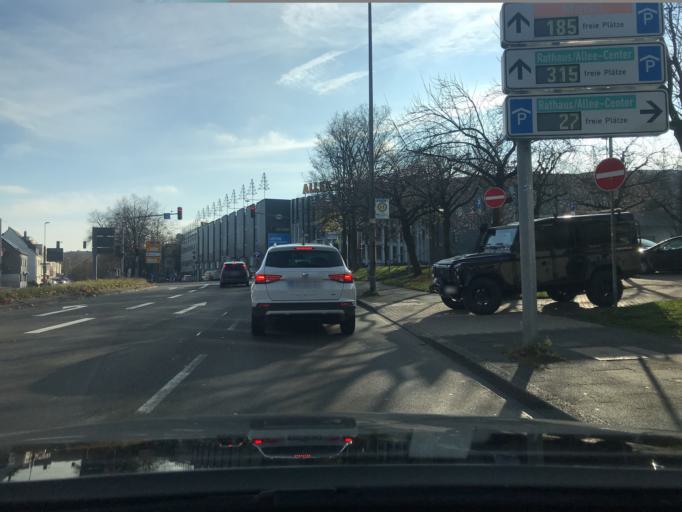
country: DE
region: North Rhine-Westphalia
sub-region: Regierungsbezirk Dusseldorf
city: Remscheid
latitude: 51.1846
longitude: 7.1867
